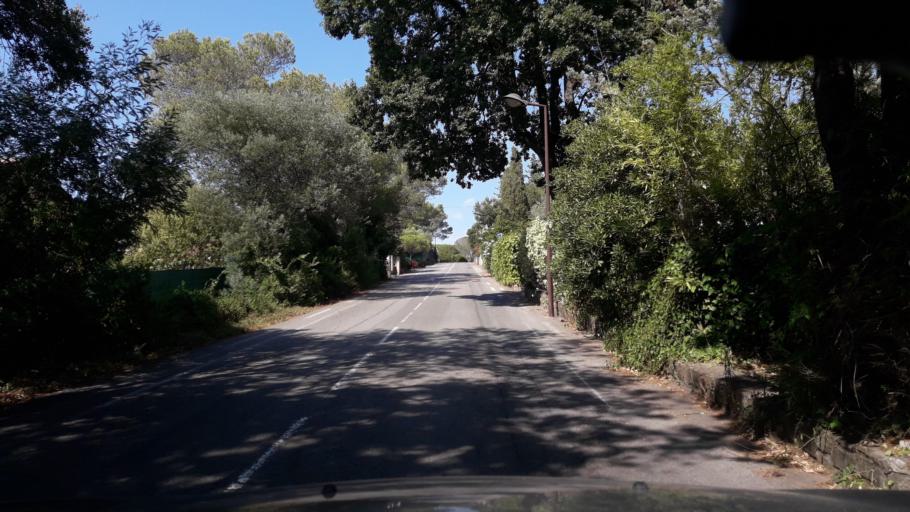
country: FR
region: Provence-Alpes-Cote d'Azur
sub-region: Departement du Var
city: Saint-Raphael
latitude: 43.4600
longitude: 6.7651
